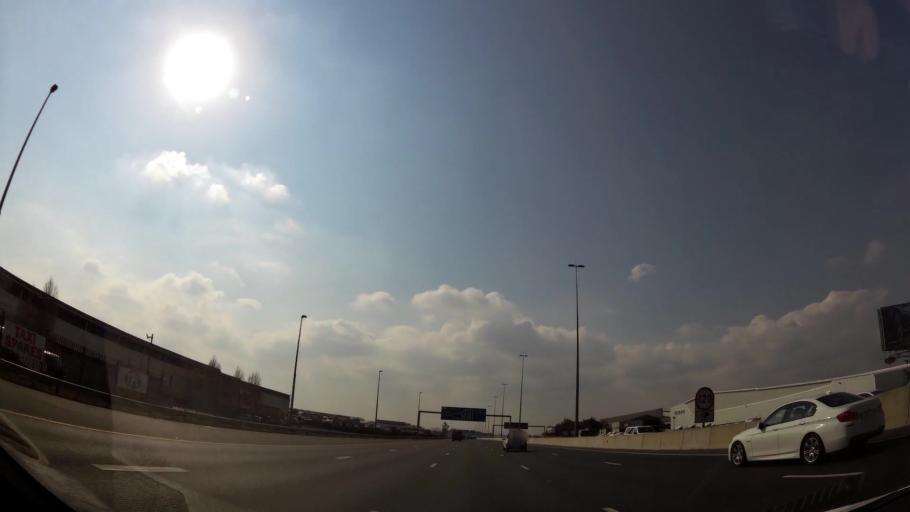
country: ZA
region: Gauteng
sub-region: Ekurhuleni Metropolitan Municipality
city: Boksburg
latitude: -26.1772
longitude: 28.2216
